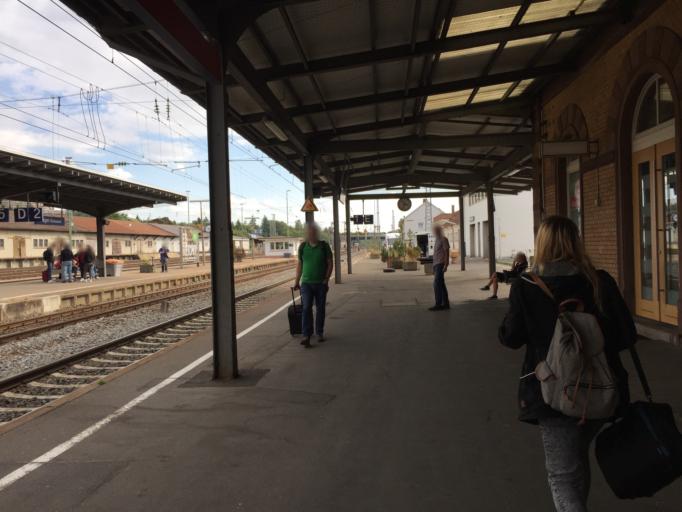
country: DE
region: Baden-Wuerttemberg
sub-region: Freiburg Region
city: Villingen-Schwenningen
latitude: 48.0576
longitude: 8.4655
